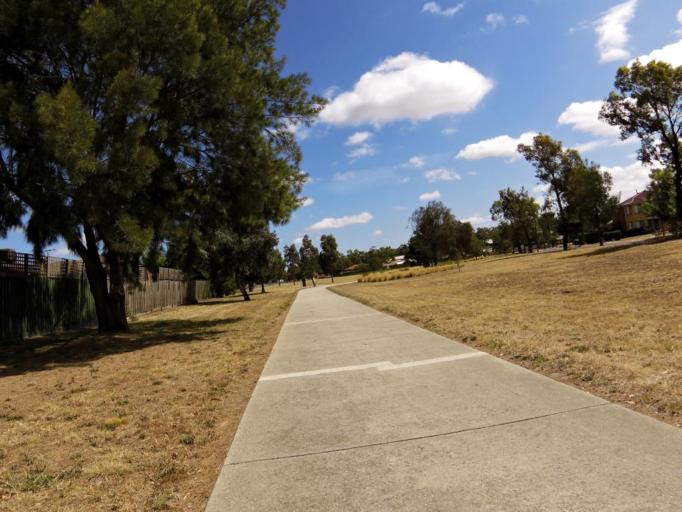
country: AU
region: Victoria
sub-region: Hume
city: Roxburgh Park
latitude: -37.6302
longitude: 144.9222
